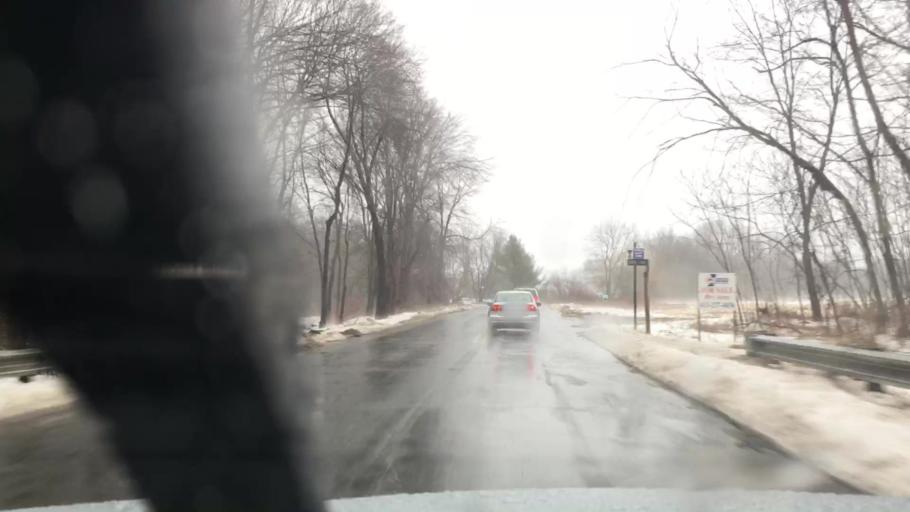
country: US
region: Massachusetts
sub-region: Hampshire County
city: Granby
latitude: 42.2214
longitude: -72.4982
